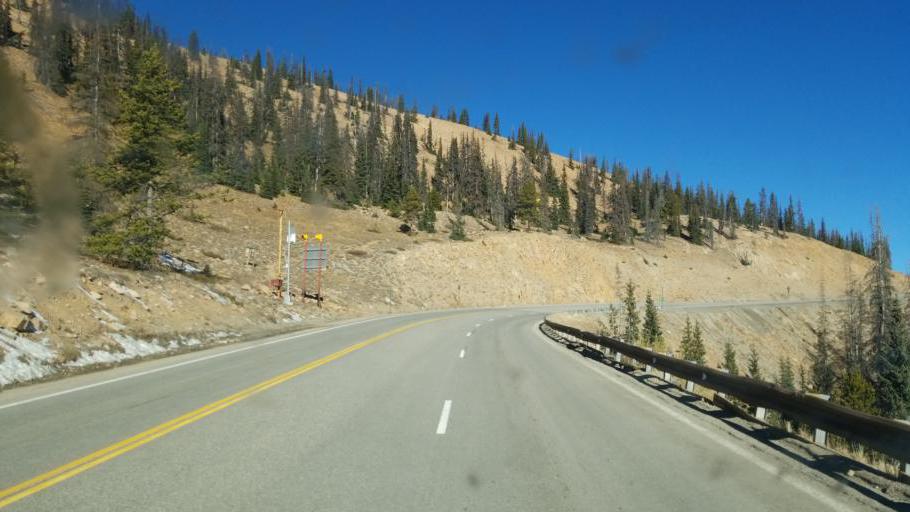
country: US
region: Colorado
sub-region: Chaffee County
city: Salida
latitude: 38.4925
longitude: -106.3264
